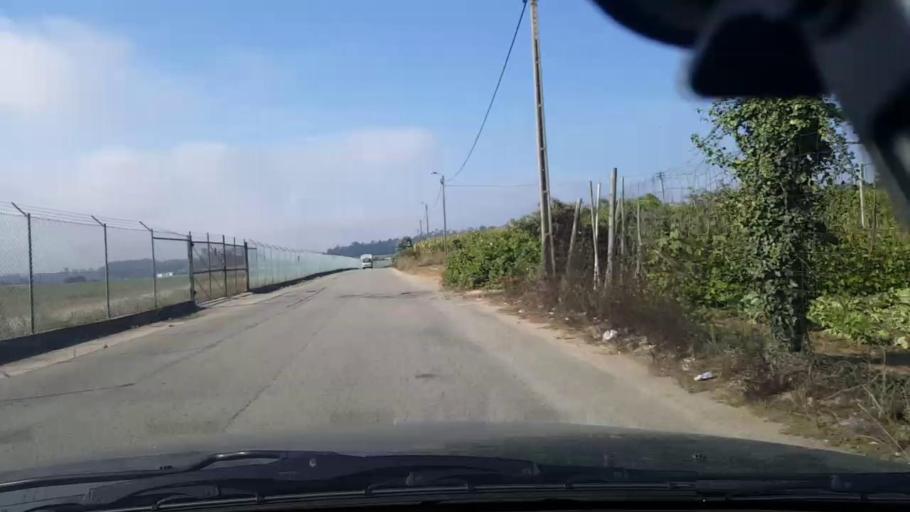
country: PT
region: Porto
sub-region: Matosinhos
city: Lavra
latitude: 41.2632
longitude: -8.6829
